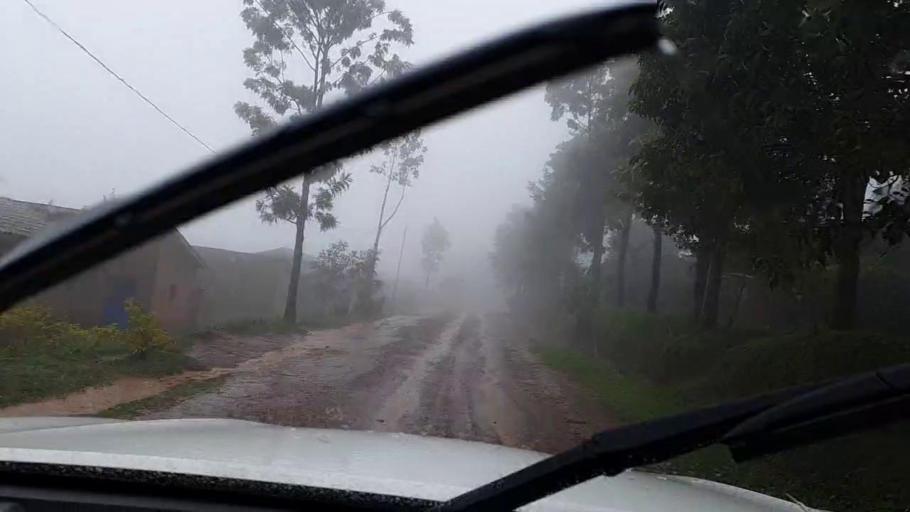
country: RW
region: Northern Province
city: Byumba
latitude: -1.7327
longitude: 30.0147
